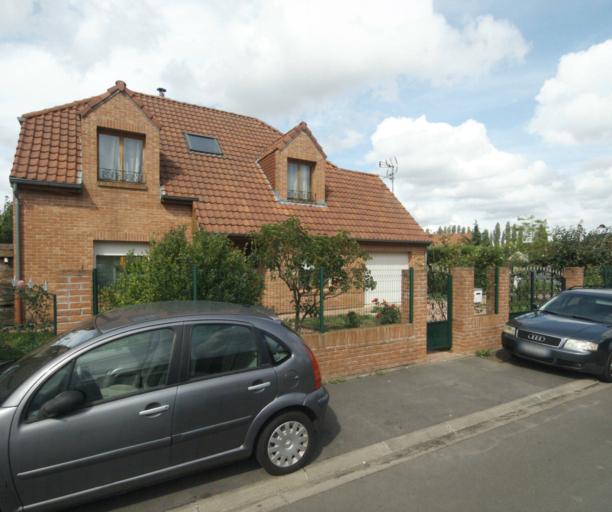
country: FR
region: Nord-Pas-de-Calais
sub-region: Departement du Nord
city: Faches-Thumesnil
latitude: 50.6009
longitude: 3.0591
